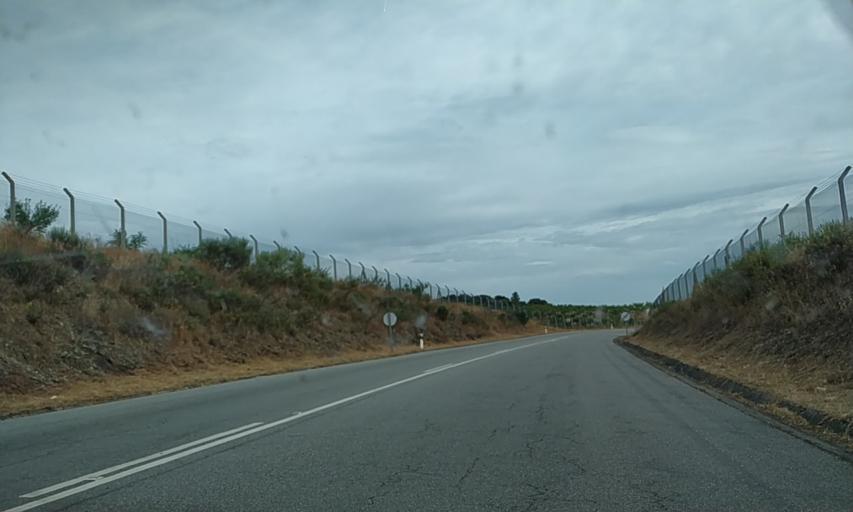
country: PT
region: Viseu
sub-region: Sao Joao da Pesqueira
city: Sao Joao da Pesqueira
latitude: 41.1249
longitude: -7.3916
